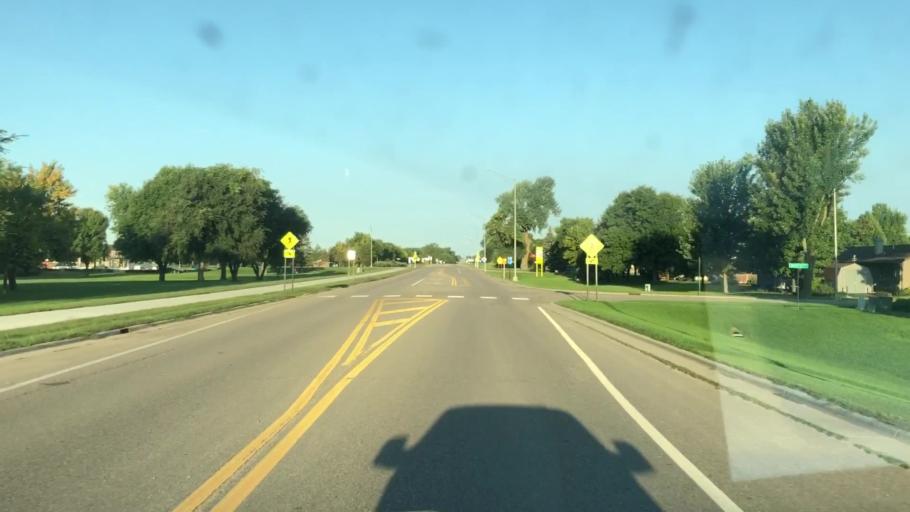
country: US
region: Minnesota
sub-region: Nobles County
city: Worthington
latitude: 43.6310
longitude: -95.6256
